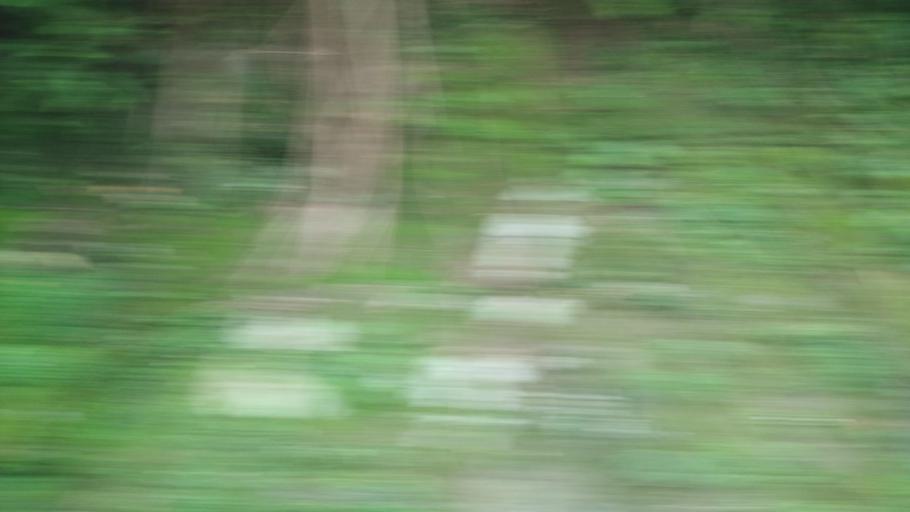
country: TW
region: Taipei
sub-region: Taipei
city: Banqiao
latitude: 24.9267
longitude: 121.4391
